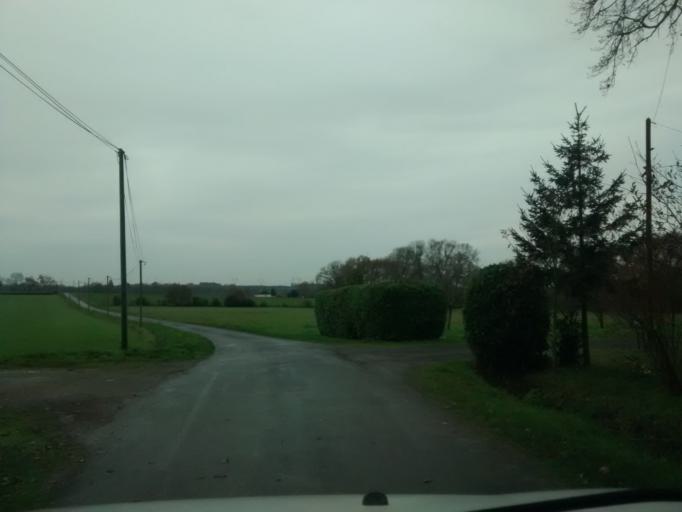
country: FR
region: Brittany
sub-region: Departement d'Ille-et-Vilaine
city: Acigne
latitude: 48.1336
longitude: -1.5540
